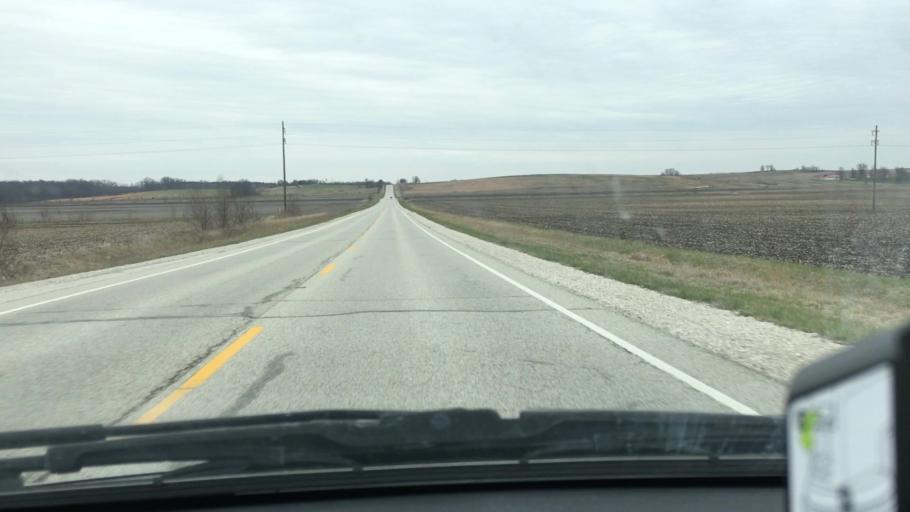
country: US
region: Indiana
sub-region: Greene County
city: Bloomfield
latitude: 39.0003
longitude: -87.0161
